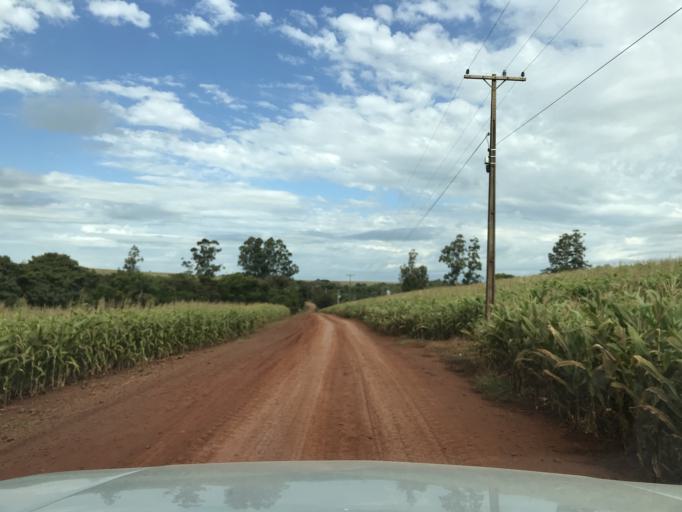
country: BR
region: Parana
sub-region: Palotina
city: Palotina
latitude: -24.3199
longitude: -53.8065
